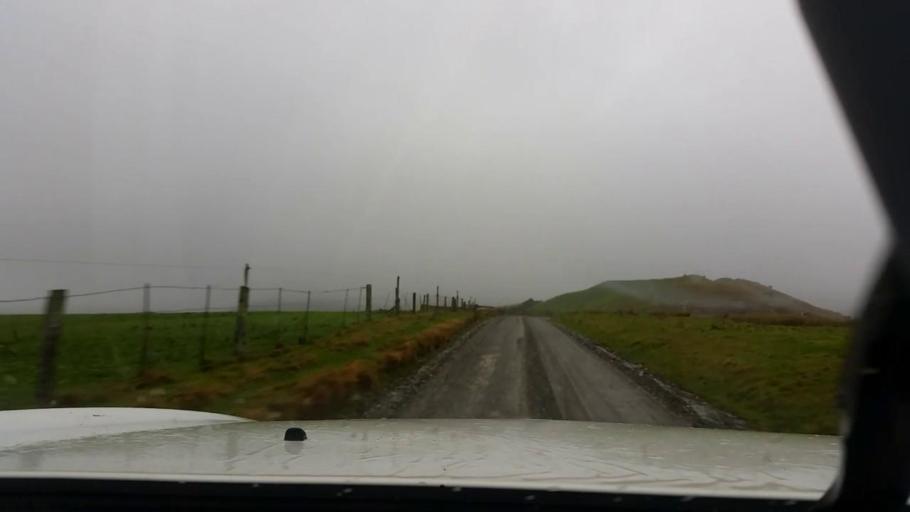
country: NZ
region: Wellington
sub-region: Masterton District
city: Masterton
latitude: -41.2508
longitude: 175.8938
